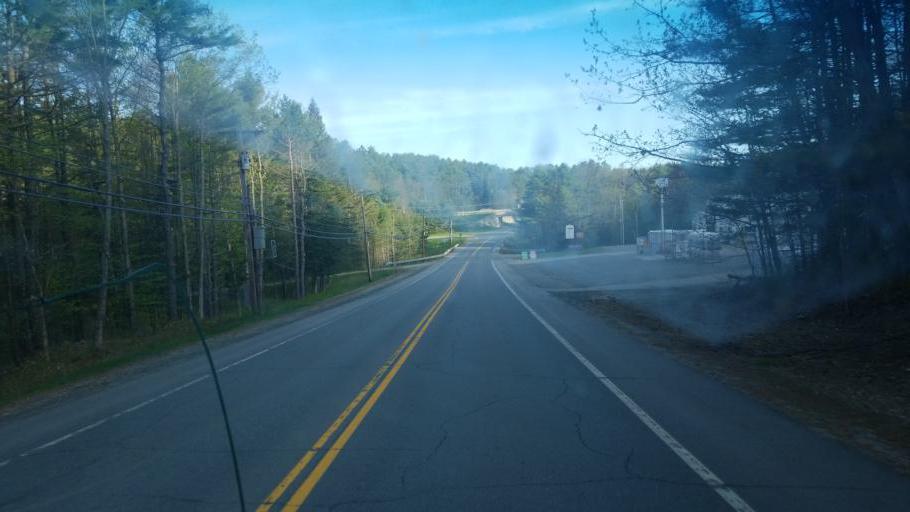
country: US
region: New Hampshire
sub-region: Grafton County
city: Littleton
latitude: 44.3145
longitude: -71.7951
